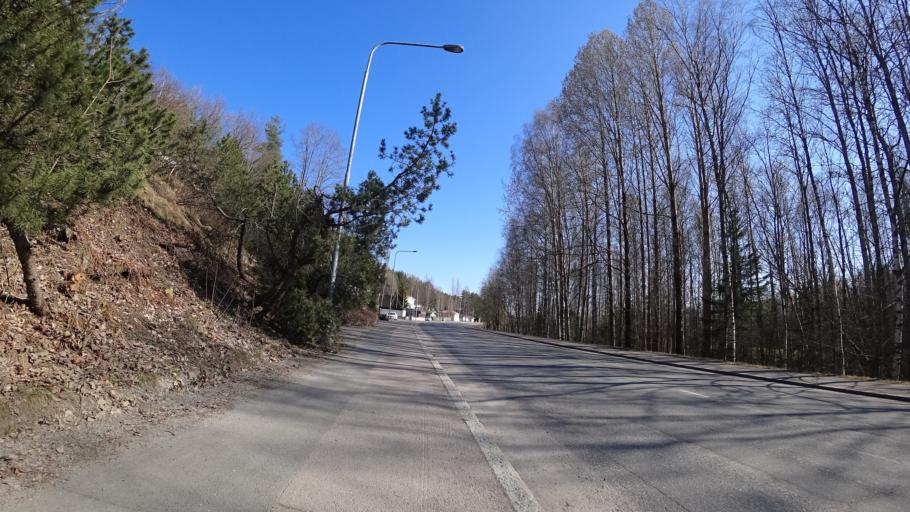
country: FI
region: Pirkanmaa
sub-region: Tampere
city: Pirkkala
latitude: 61.5178
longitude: 23.6471
